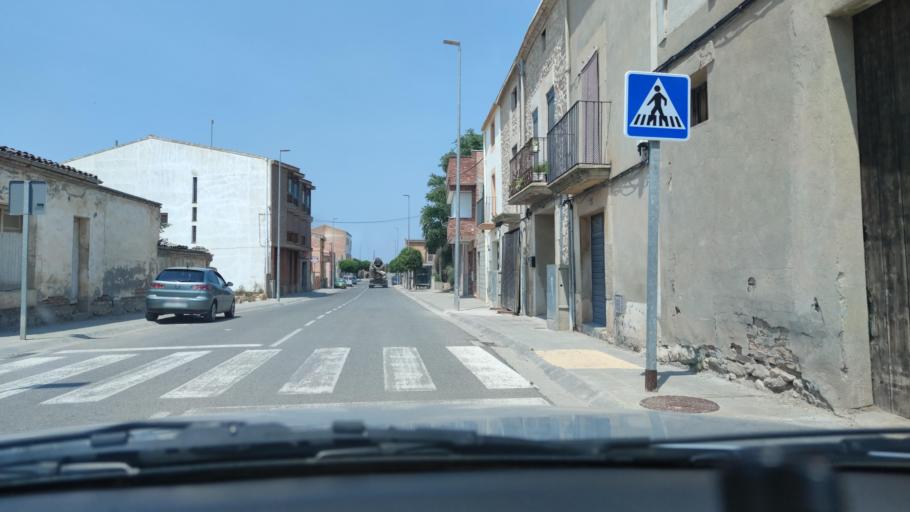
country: ES
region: Catalonia
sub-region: Provincia de Lleida
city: Bellpuig
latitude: 41.6073
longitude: 1.0367
